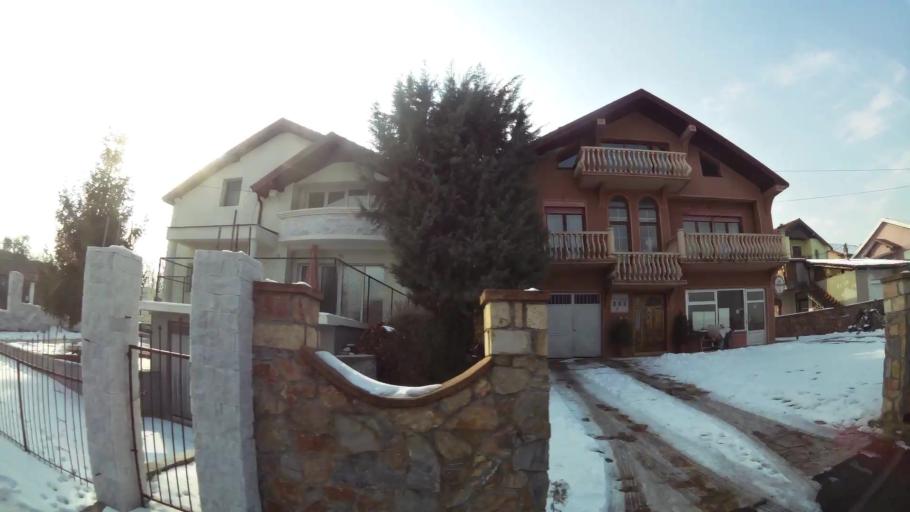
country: MK
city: Creshevo
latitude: 42.0083
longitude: 21.4985
